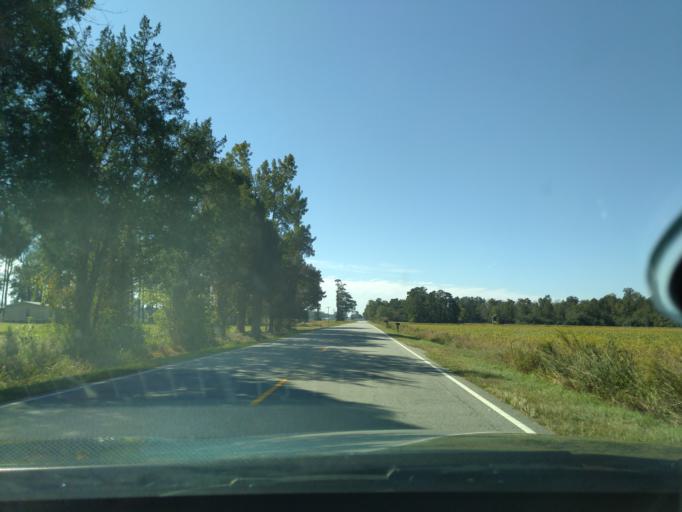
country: US
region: North Carolina
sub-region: Washington County
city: Plymouth
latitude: 35.7269
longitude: -76.7489
